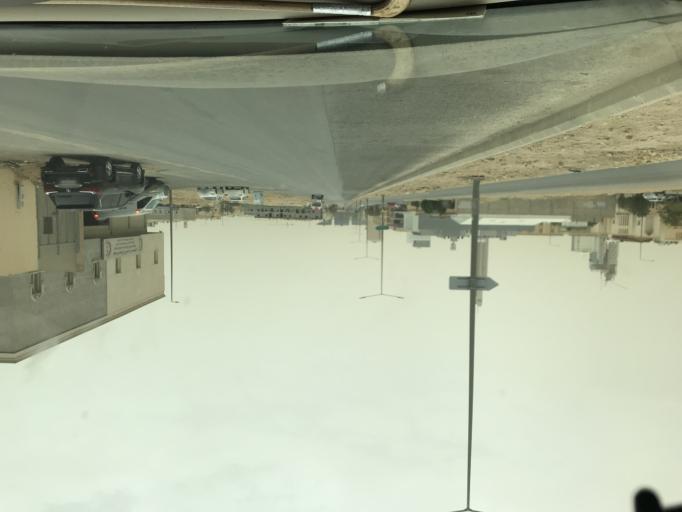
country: SA
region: Ar Riyad
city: Riyadh
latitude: 24.8131
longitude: 46.6081
